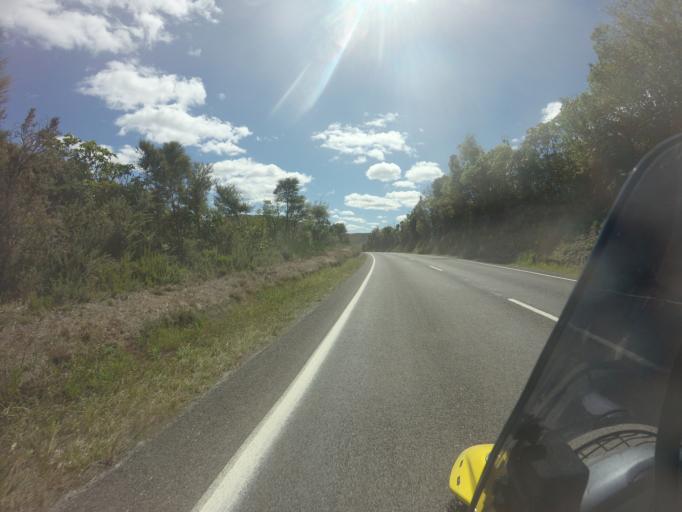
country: NZ
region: Bay of Plenty
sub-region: Kawerau District
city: Kawerau
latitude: -38.1613
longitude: 176.8047
